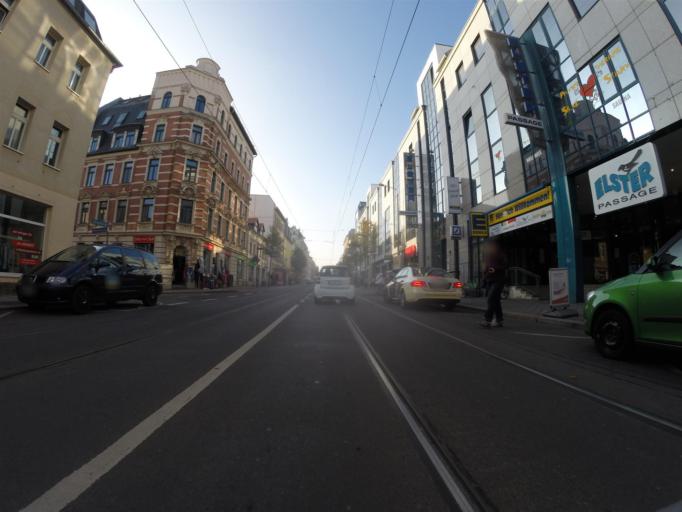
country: DE
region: Saxony
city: Leipzig
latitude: 51.3296
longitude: 12.3370
